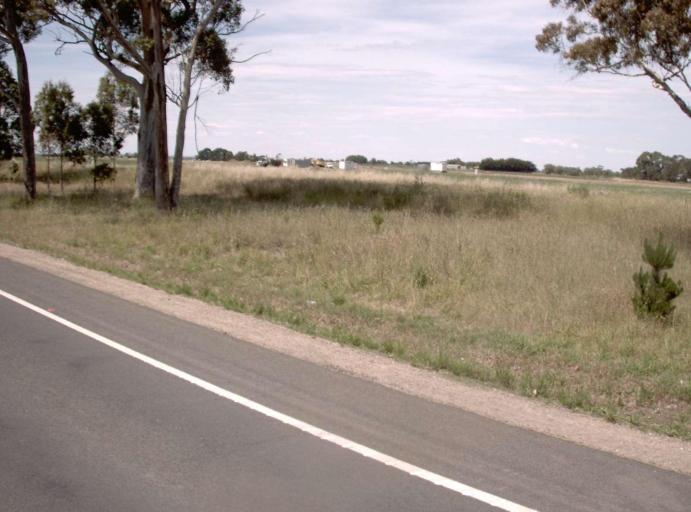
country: AU
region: Victoria
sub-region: Wellington
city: Sale
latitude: -38.0850
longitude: 147.0706
